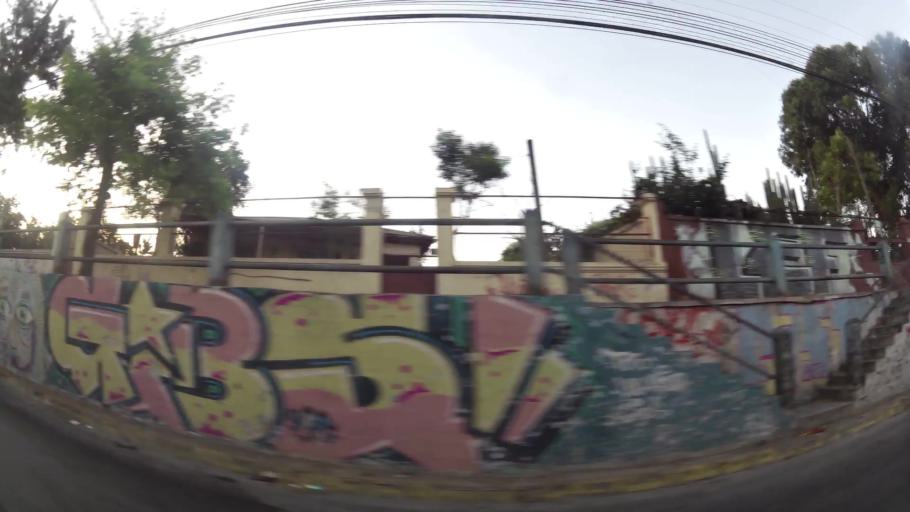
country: CL
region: Santiago Metropolitan
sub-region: Provincia de Maipo
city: San Bernardo
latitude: -33.5841
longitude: -70.6980
